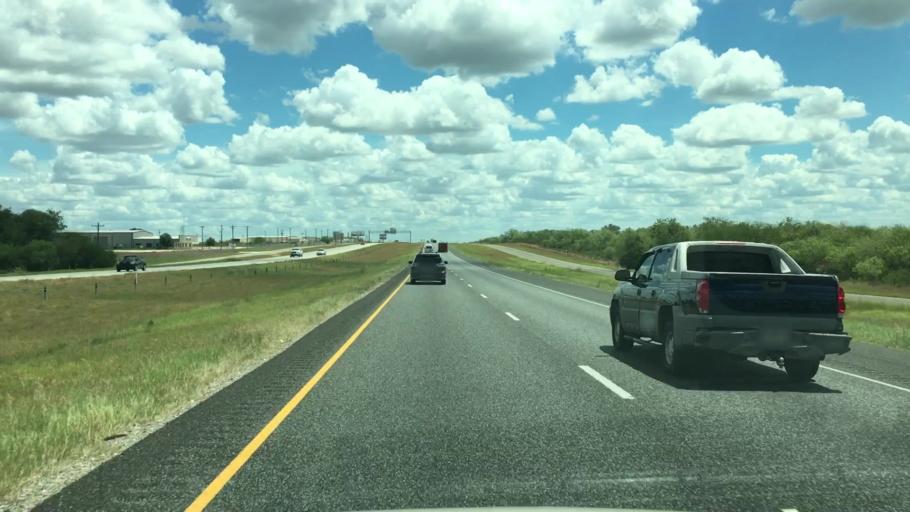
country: US
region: Texas
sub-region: Atascosa County
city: Pleasanton
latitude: 28.8961
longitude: -98.4157
